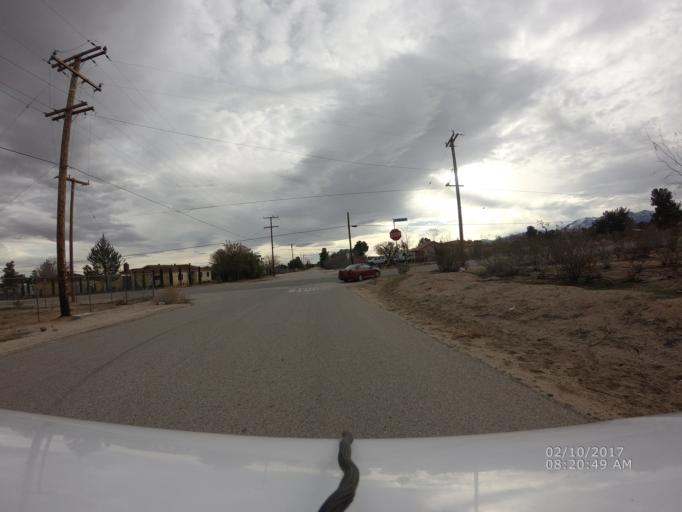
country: US
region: California
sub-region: Los Angeles County
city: Littlerock
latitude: 34.5028
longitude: -117.9056
